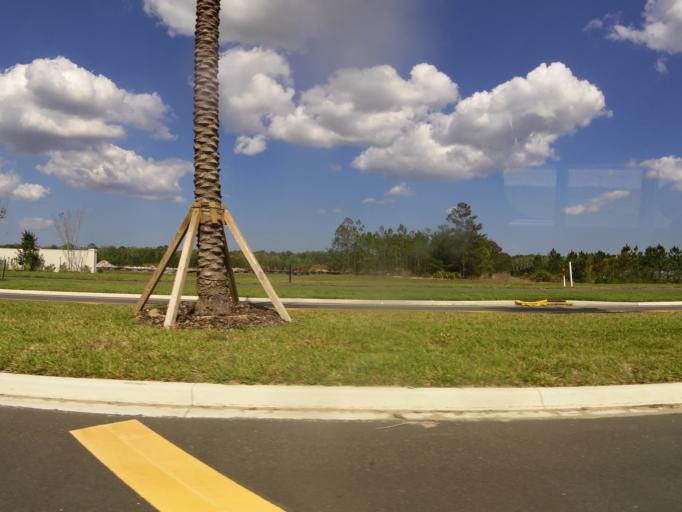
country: US
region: Florida
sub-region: Saint Johns County
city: Palm Valley
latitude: 30.1920
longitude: -81.5052
